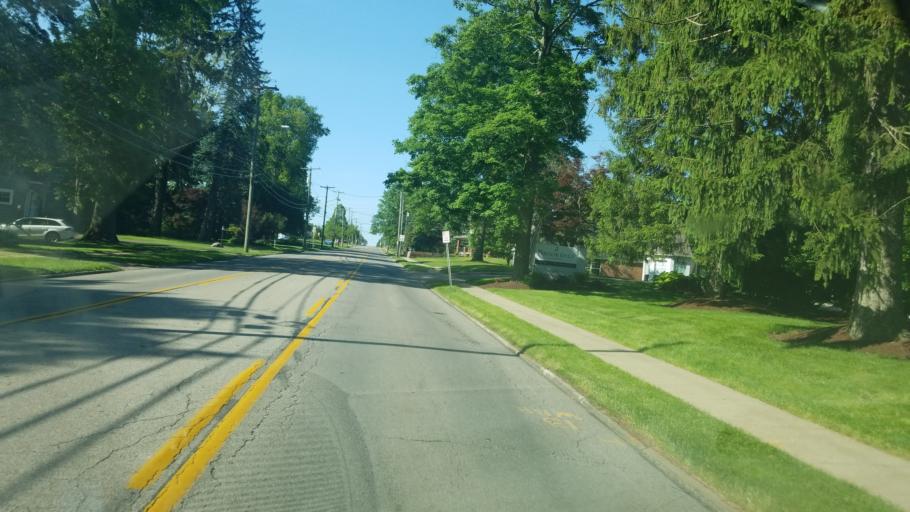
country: US
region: Ohio
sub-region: Wayne County
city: Wooster
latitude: 40.8176
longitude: -81.9366
